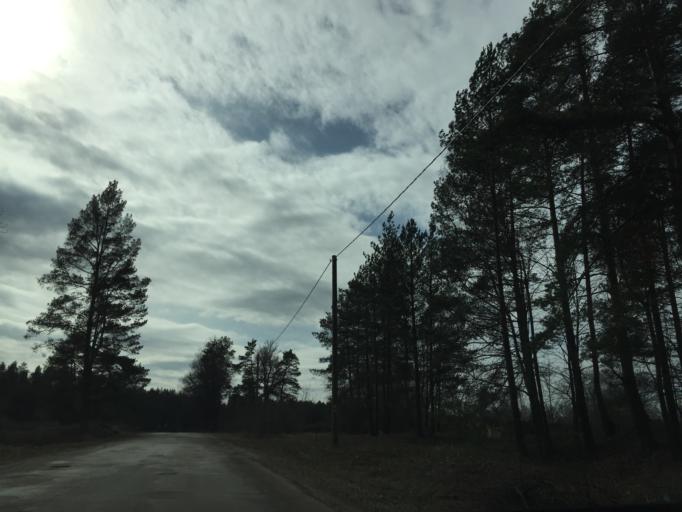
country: LV
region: Garkalne
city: Garkalne
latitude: 57.0686
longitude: 24.4160
